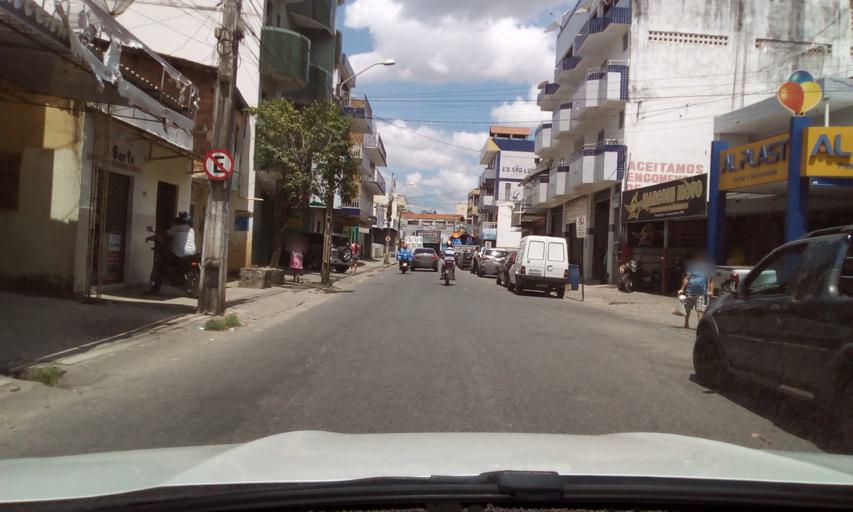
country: BR
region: Paraiba
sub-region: Guarabira
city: Guarabira
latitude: -6.8538
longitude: -35.4936
